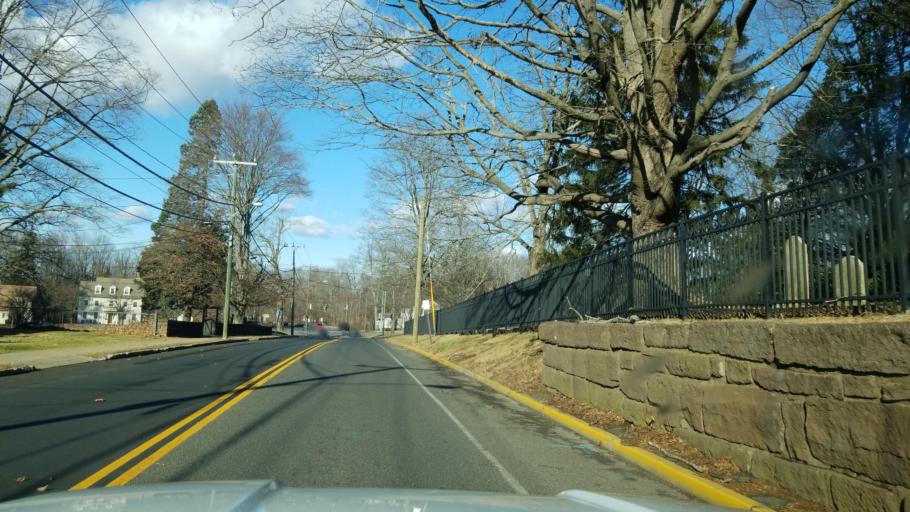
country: US
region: Connecticut
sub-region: Middlesex County
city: Middletown
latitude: 41.5576
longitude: -72.6611
